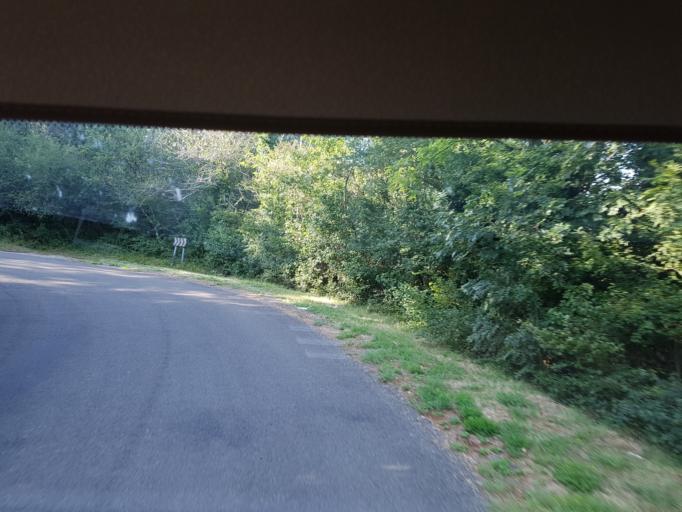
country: FR
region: Rhone-Alpes
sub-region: Departement de l'Ain
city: Poncin
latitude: 46.1389
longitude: 5.4273
